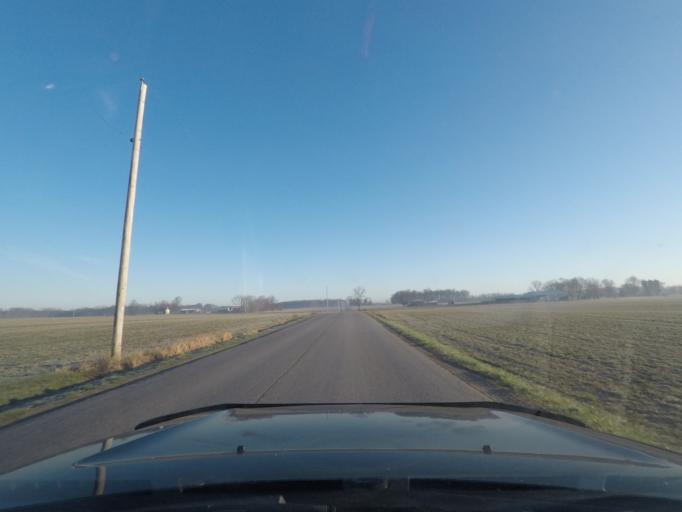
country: US
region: Indiana
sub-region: Elkhart County
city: Dunlap
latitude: 41.5628
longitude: -85.9249
